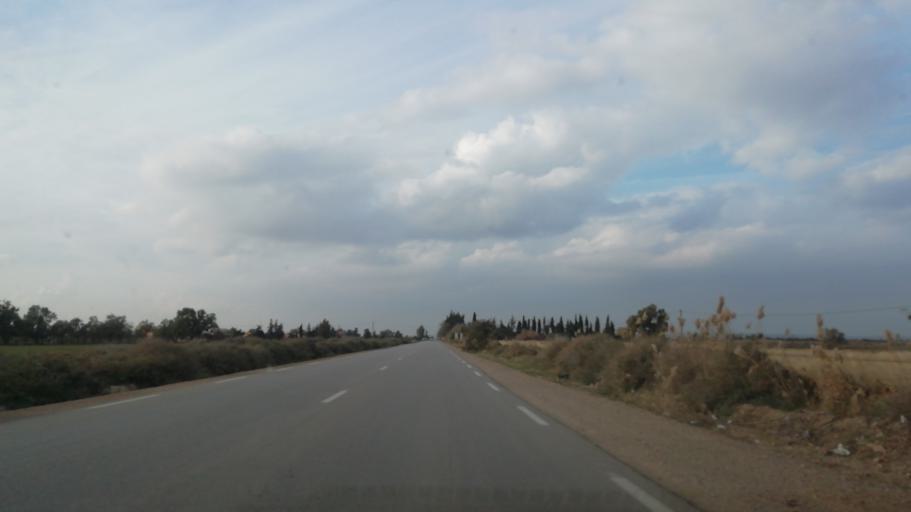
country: DZ
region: Mascara
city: Sig
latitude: 35.6755
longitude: -0.0064
